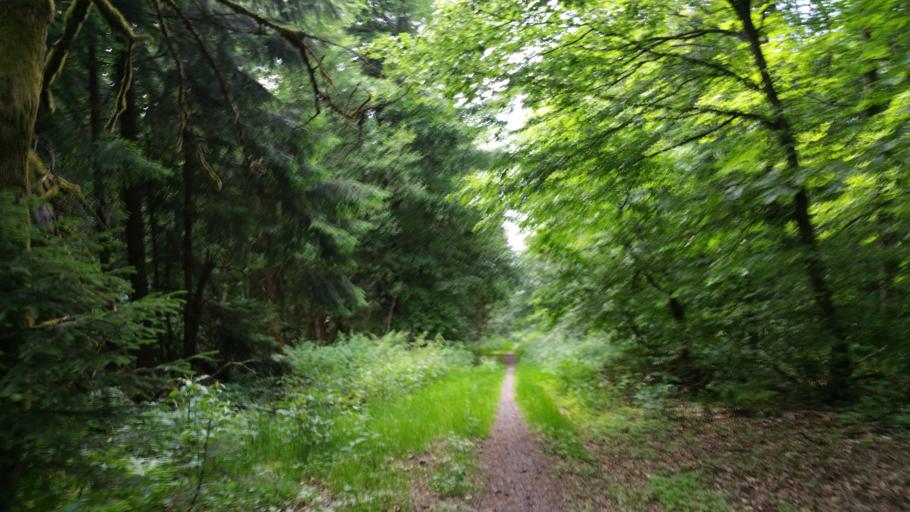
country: DE
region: Bavaria
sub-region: Upper Franconia
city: Marktleuthen
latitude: 50.1831
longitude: 12.0191
